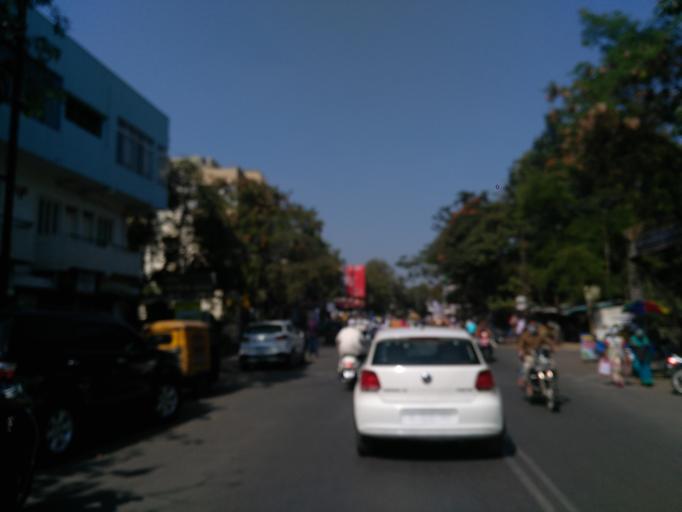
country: IN
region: Maharashtra
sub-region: Pune Division
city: Pune
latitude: 18.4907
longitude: 73.8499
